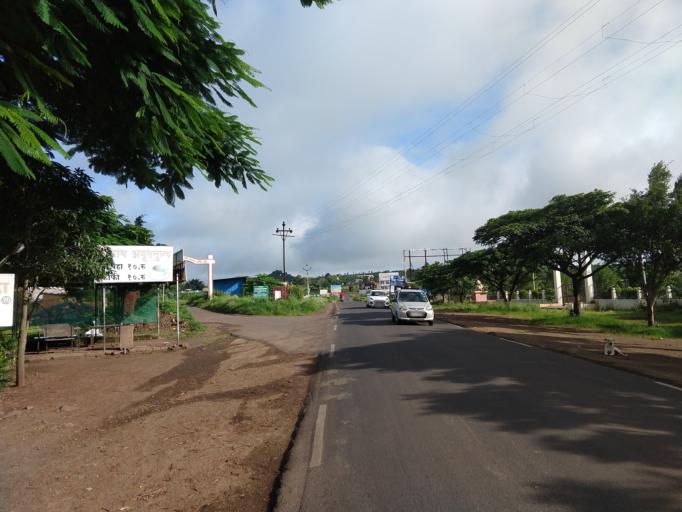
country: IN
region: Maharashtra
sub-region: Pune Division
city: Khed
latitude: 18.3960
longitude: 73.9153
